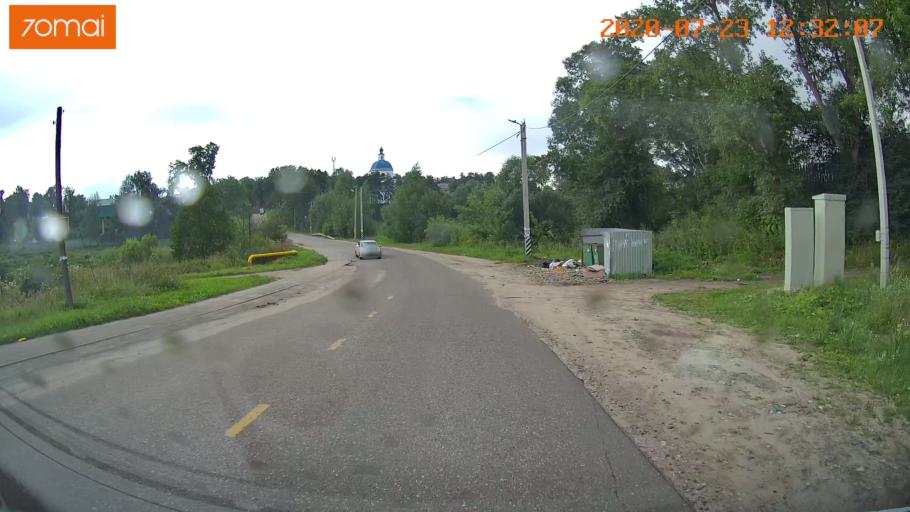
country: RU
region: Ivanovo
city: Bogorodskoye
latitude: 57.0456
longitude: 41.0106
